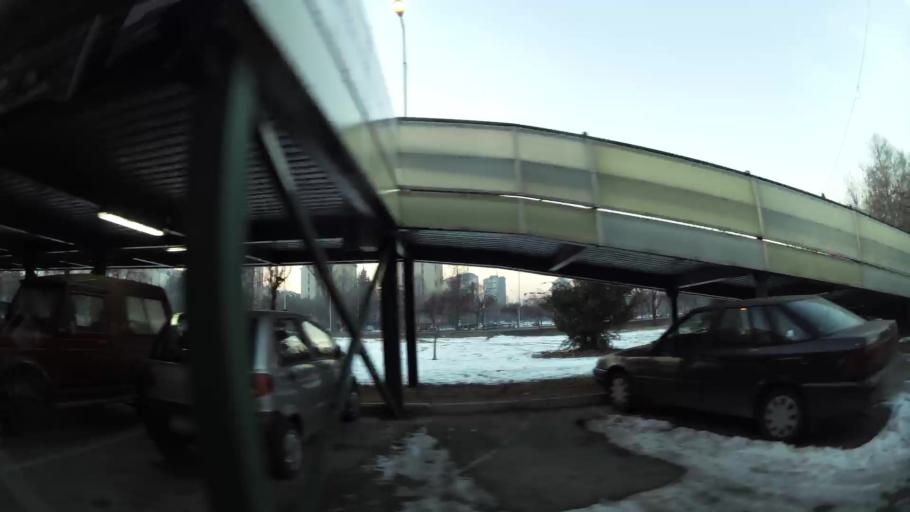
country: MK
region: Kisela Voda
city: Usje
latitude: 41.9850
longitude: 21.4734
